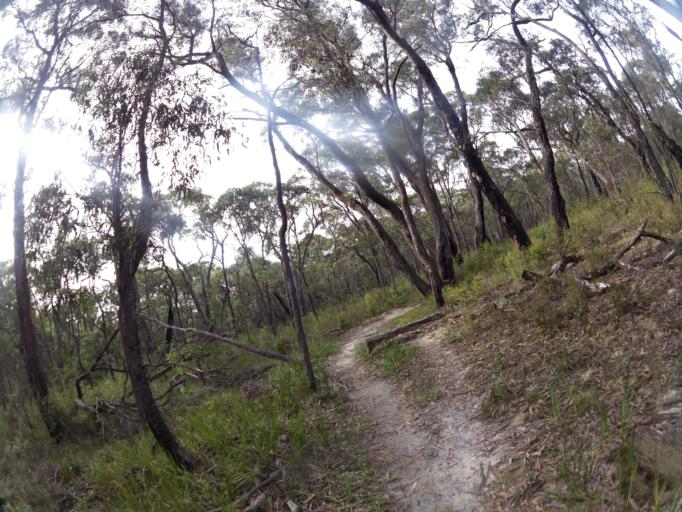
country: AU
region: Victoria
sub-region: Colac-Otway
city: Colac
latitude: -38.4897
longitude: 143.7017
